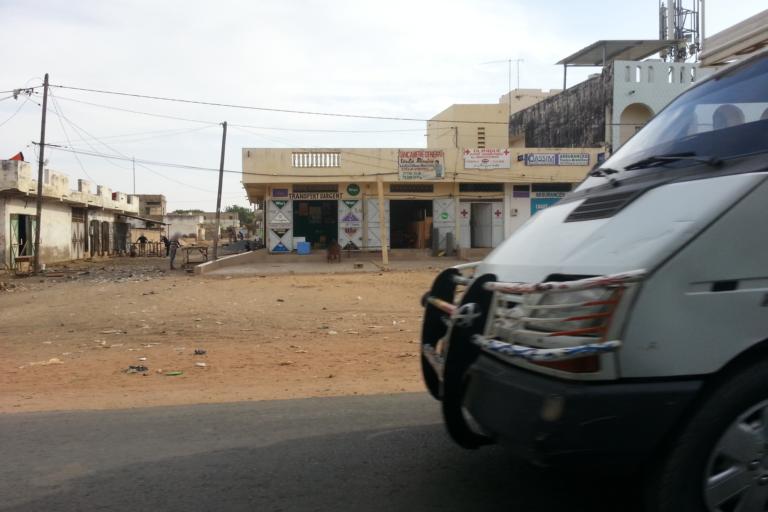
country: SN
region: Diourbel
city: Touba
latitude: 14.8795
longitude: -15.8979
